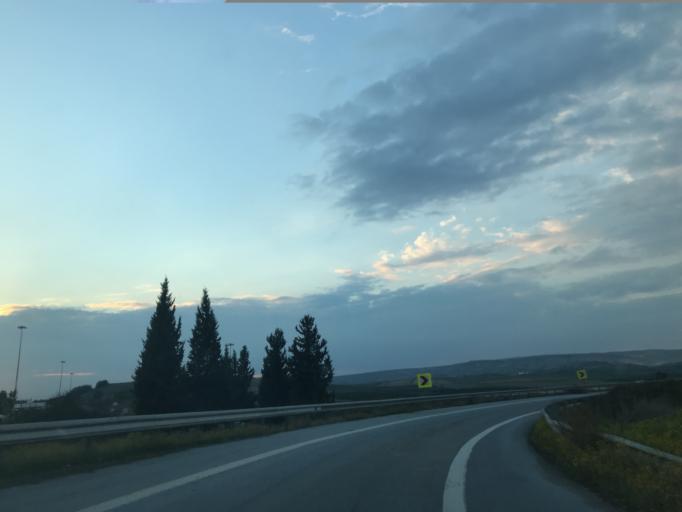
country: TR
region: Mersin
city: Yenice
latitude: 37.0079
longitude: 34.9628
